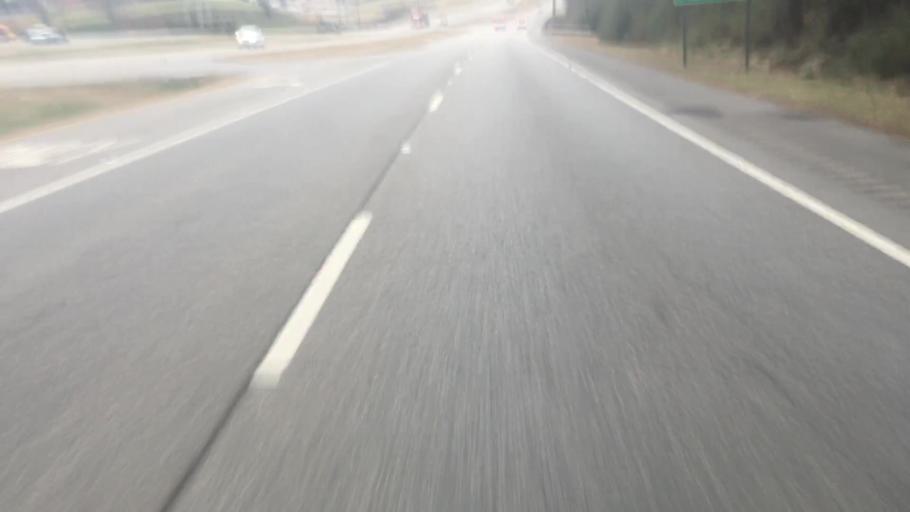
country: US
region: Alabama
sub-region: Walker County
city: Sumiton
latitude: 33.7469
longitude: -87.0518
